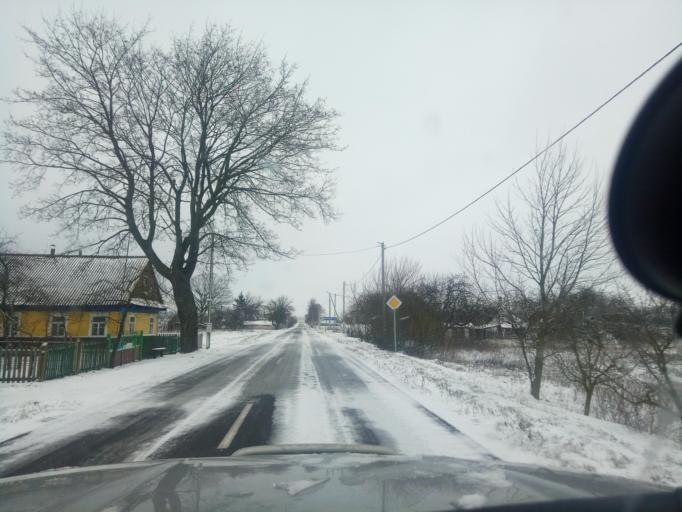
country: BY
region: Minsk
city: Klyetsk
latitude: 53.0532
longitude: 26.7719
